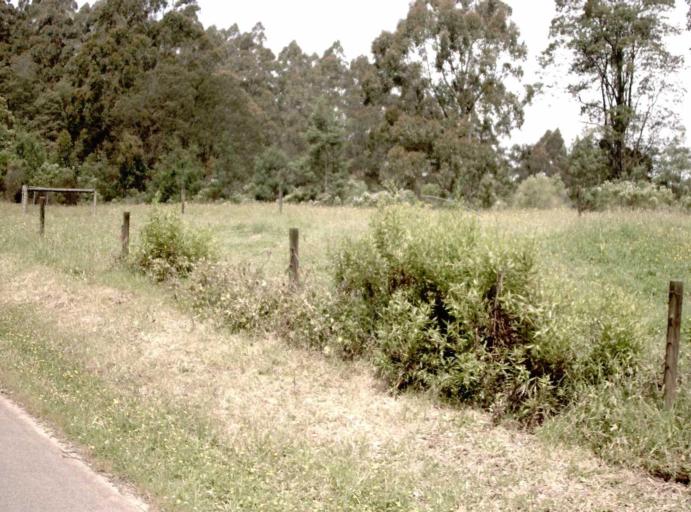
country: AU
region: Victoria
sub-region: Latrobe
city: Traralgon
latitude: -38.4241
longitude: 146.5960
